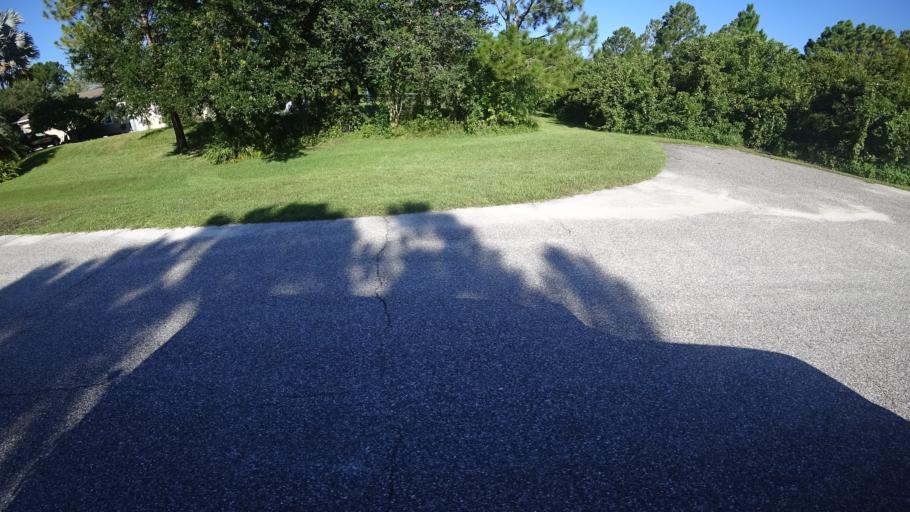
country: US
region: Florida
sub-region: Sarasota County
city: The Meadows
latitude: 27.4062
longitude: -82.3121
